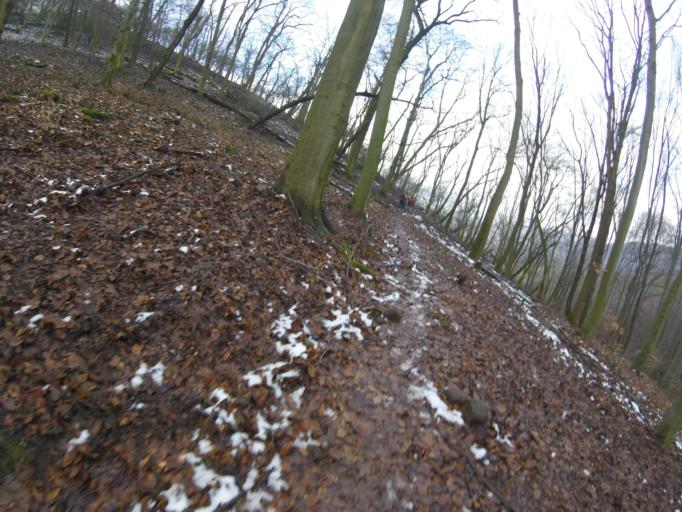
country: HU
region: Pest
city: Visegrad
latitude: 47.7648
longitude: 18.9884
